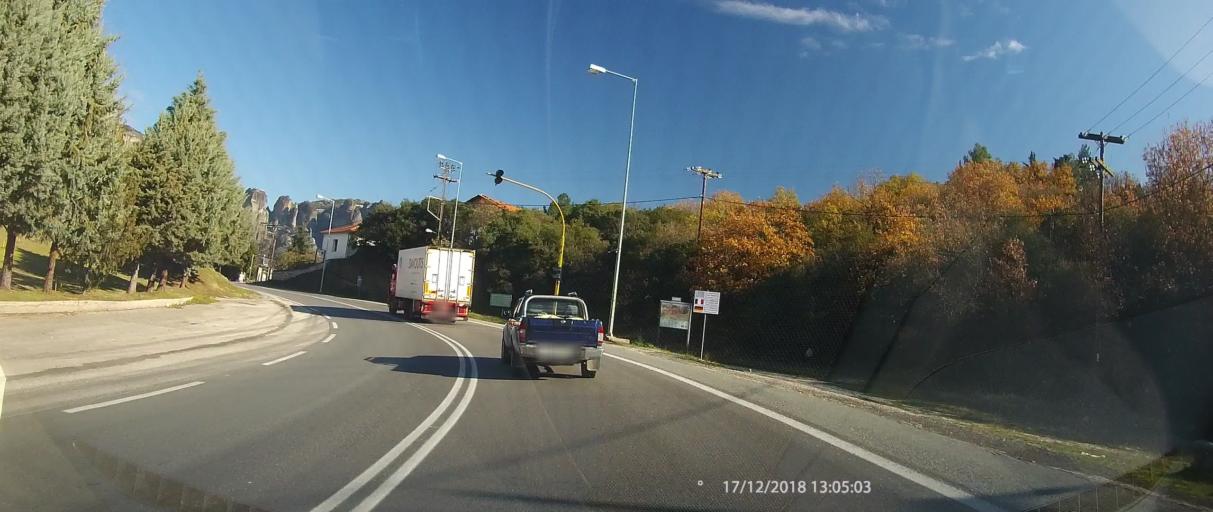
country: GR
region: Thessaly
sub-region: Trikala
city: Kalampaka
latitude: 39.7021
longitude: 21.6149
